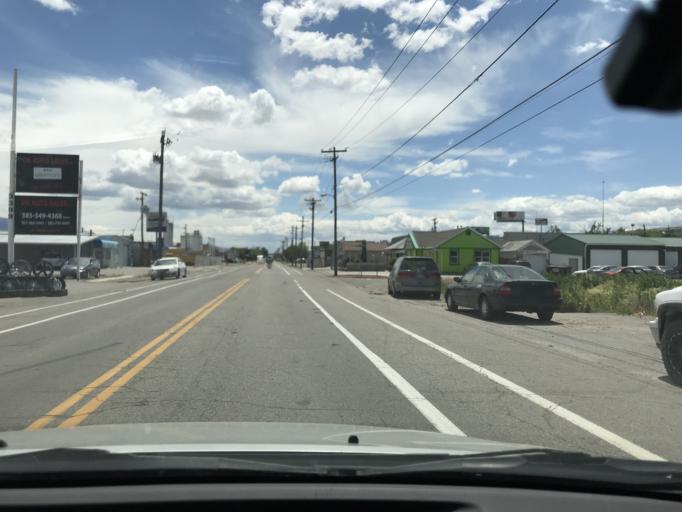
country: US
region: Utah
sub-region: Salt Lake County
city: Centerfield
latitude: 40.6981
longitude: -111.8998
